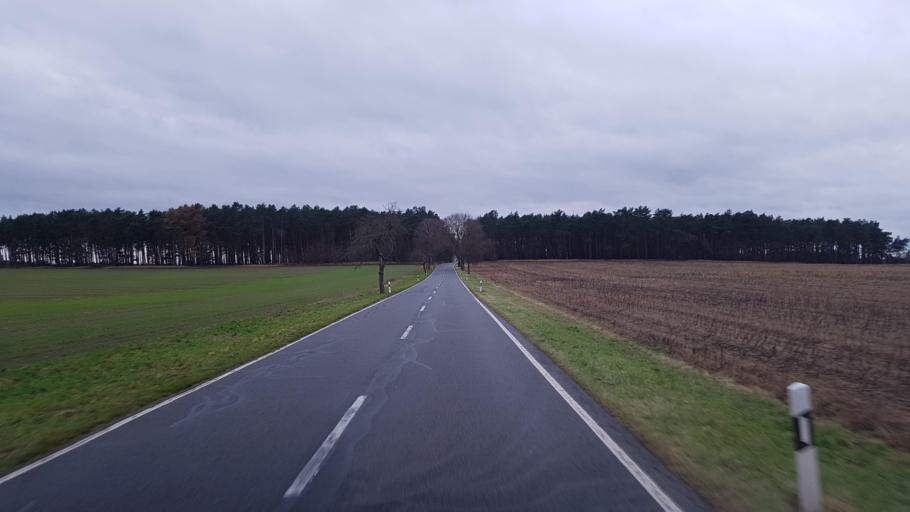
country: DE
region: Brandenburg
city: Wendisch Rietz
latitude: 52.0728
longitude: 14.0509
